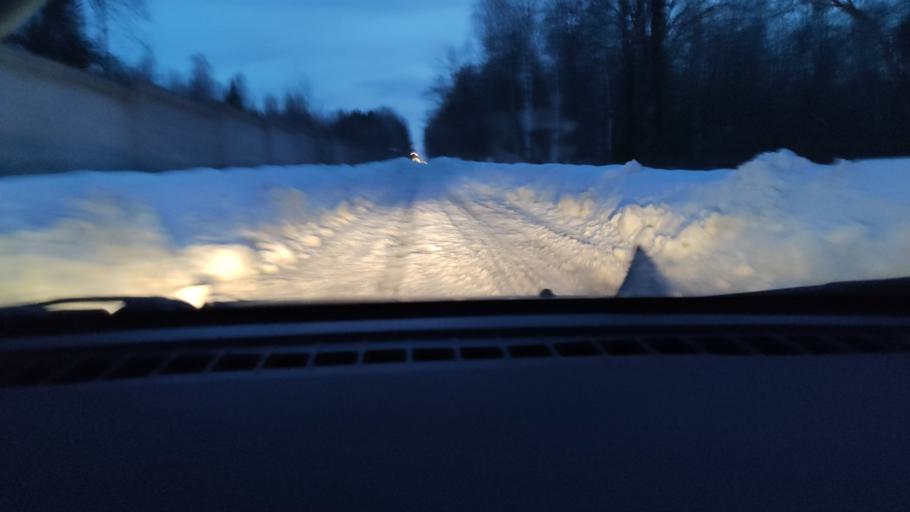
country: RU
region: Perm
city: Kondratovo
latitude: 58.0684
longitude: 56.1270
